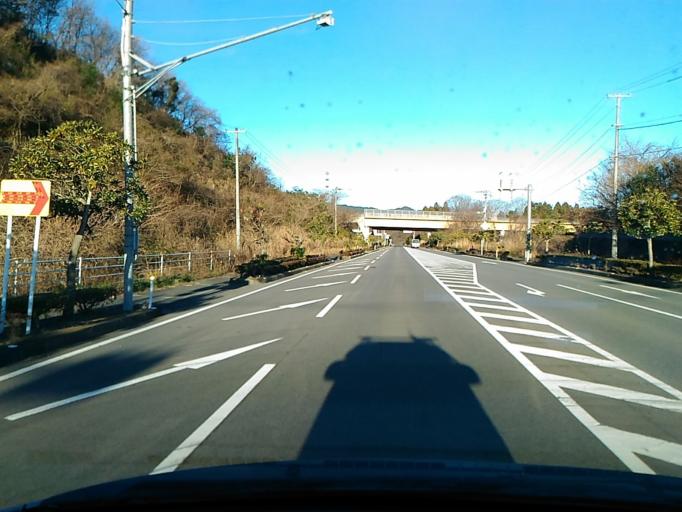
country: JP
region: Ibaraki
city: Kitaibaraki
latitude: 36.9048
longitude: 140.7531
